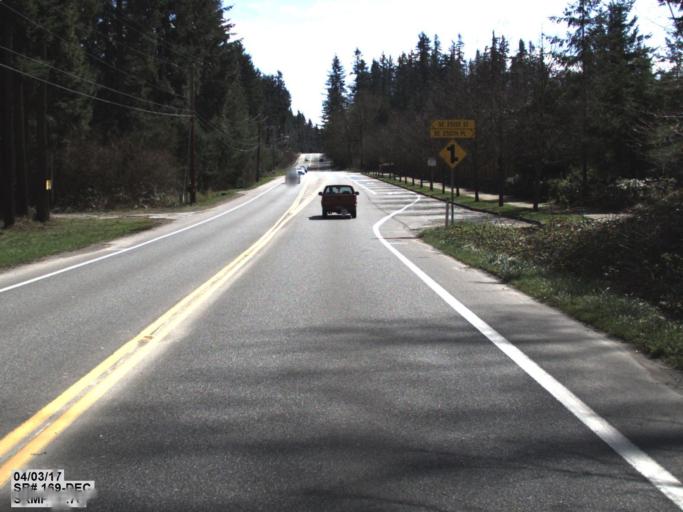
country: US
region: Washington
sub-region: King County
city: Maple Valley
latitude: 47.3799
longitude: -122.0287
